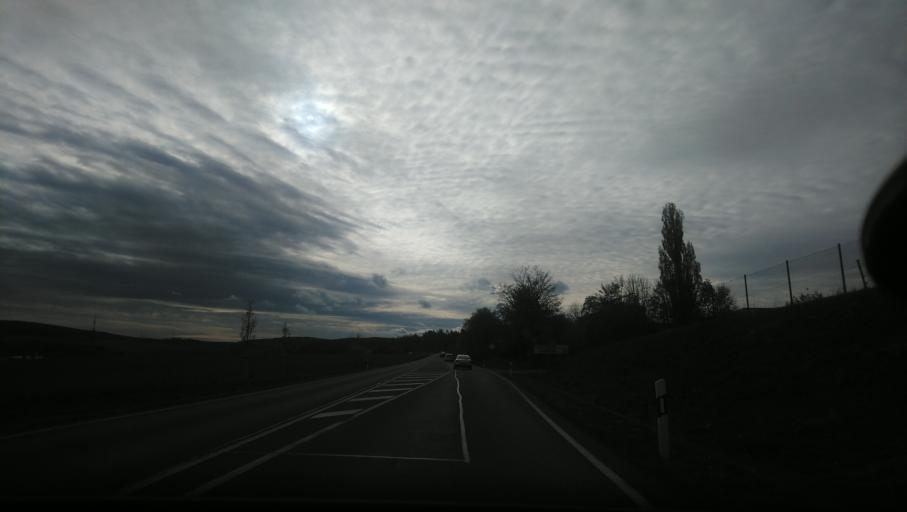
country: DE
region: Saxony
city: Dorfchemnitz
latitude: 50.6597
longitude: 12.8093
